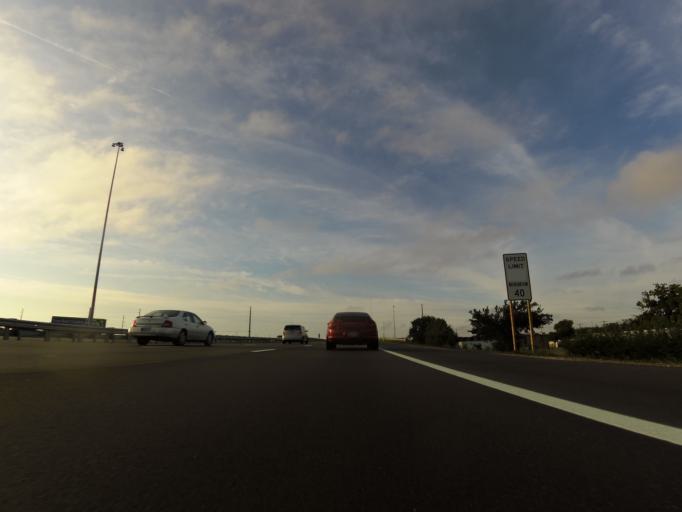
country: US
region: Kansas
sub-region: Sedgwick County
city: Park City
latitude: 37.7541
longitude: -97.3201
